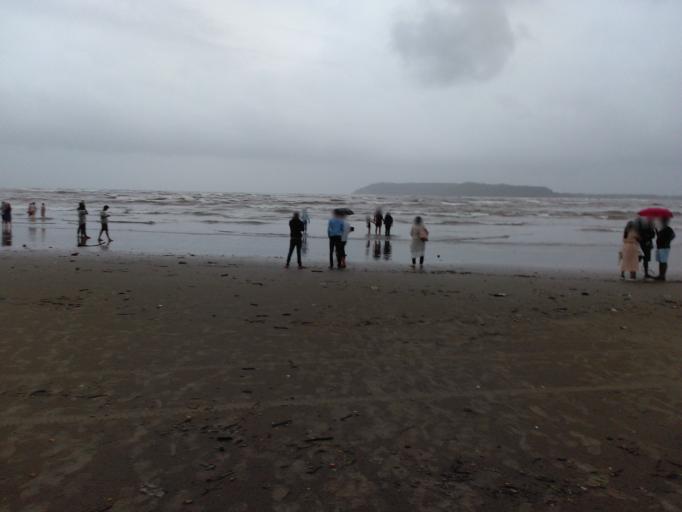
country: IN
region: Goa
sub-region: North Goa
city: Panaji
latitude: 15.4828
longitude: 73.8073
